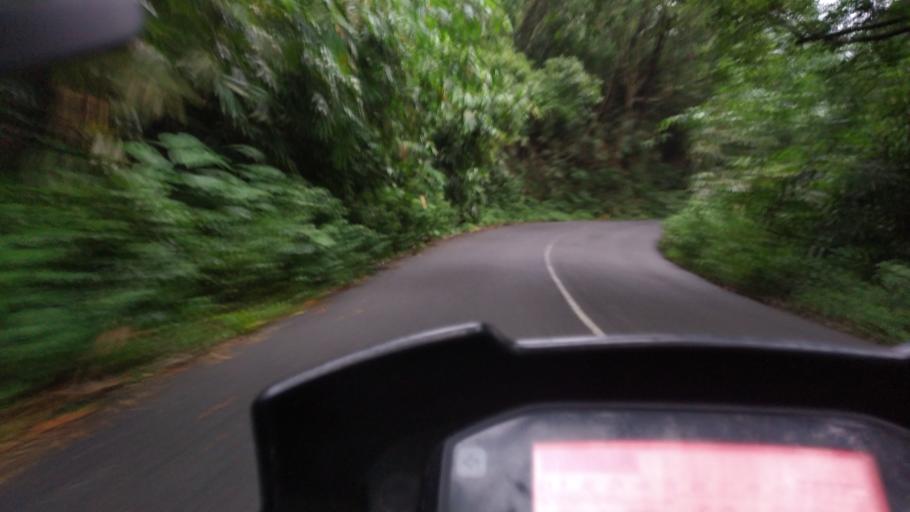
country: IN
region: Kerala
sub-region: Idukki
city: Kuttampuzha
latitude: 10.0638
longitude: 76.7933
